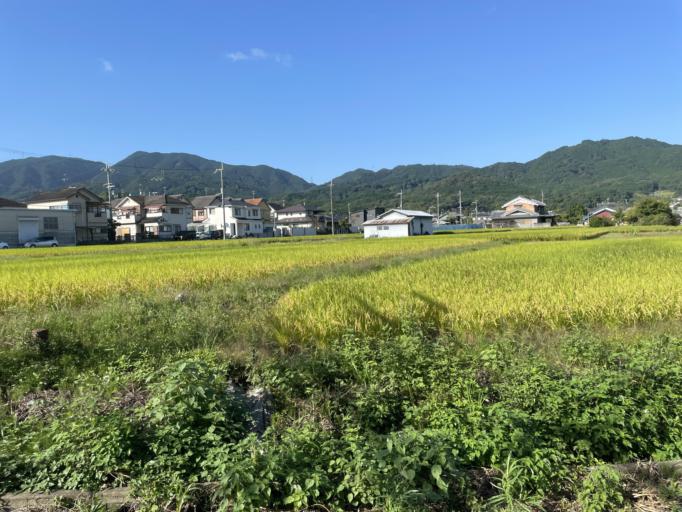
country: JP
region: Nara
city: Gose
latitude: 34.5179
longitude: 135.7048
